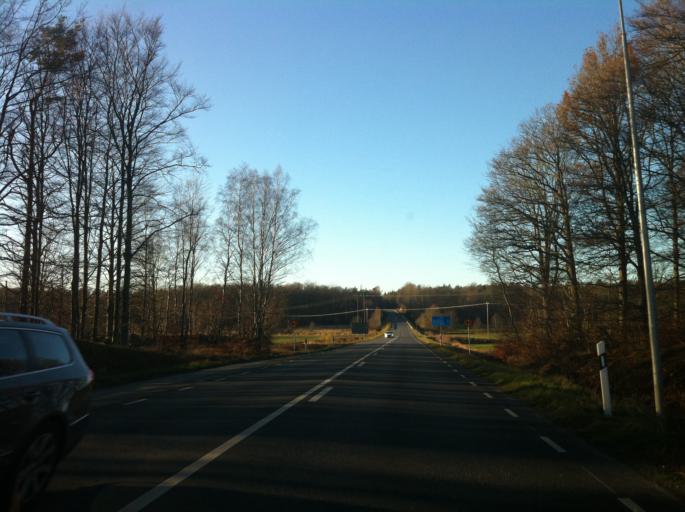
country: SE
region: Blekinge
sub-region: Karlshamns Kommun
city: Morrum
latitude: 56.1685
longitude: 14.6733
